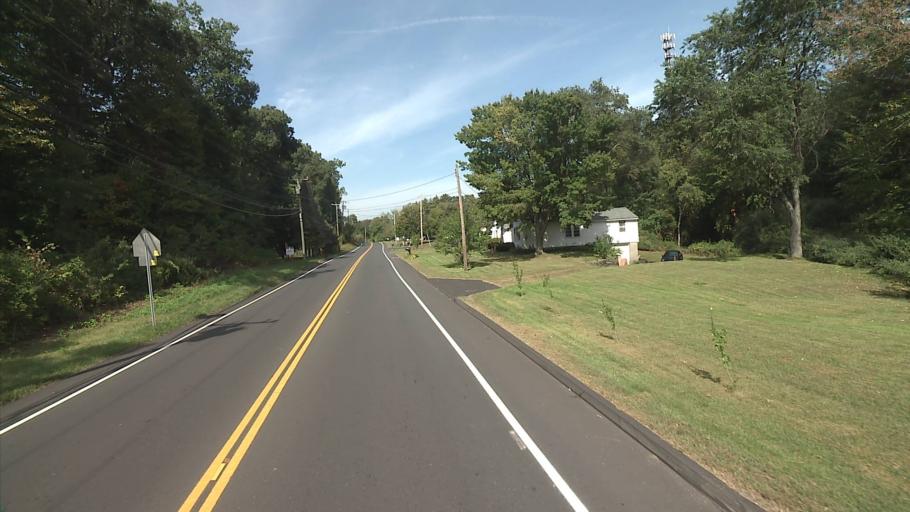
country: US
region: Connecticut
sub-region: Fairfield County
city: Newtown
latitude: 41.4111
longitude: -73.2697
